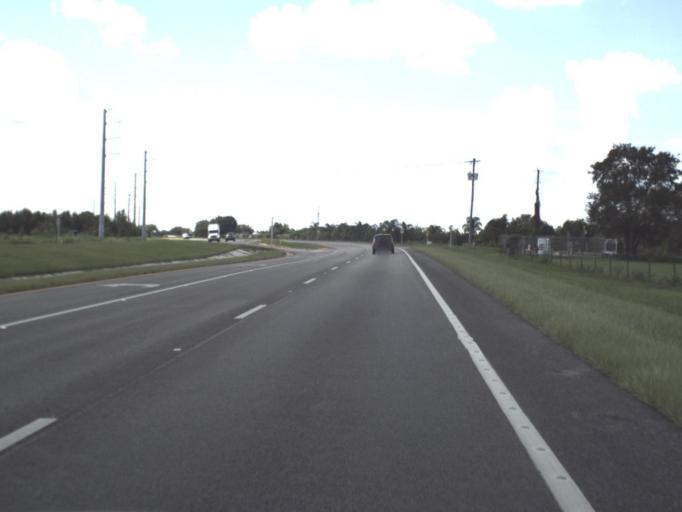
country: US
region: Florida
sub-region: Charlotte County
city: Harbour Heights
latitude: 27.0799
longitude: -81.9575
